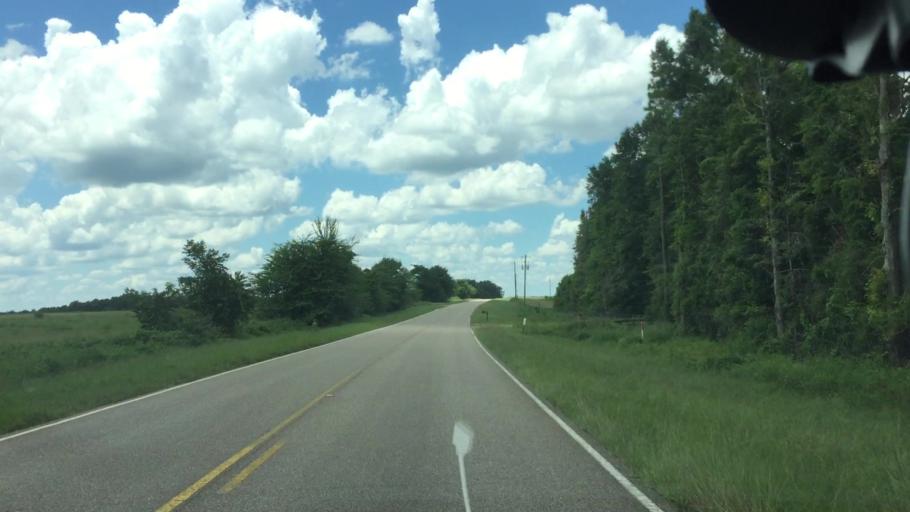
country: US
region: Alabama
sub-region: Coffee County
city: New Brockton
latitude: 31.4143
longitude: -85.8685
